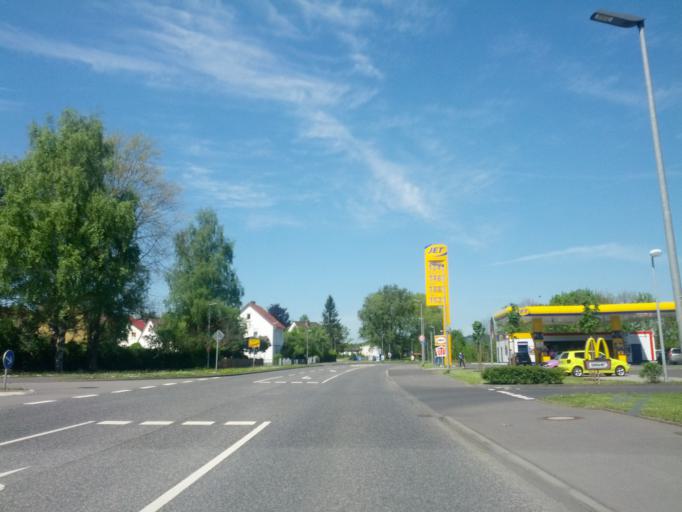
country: DE
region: Hesse
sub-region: Regierungsbezirk Kassel
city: Eschwege
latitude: 51.1971
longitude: 10.0182
